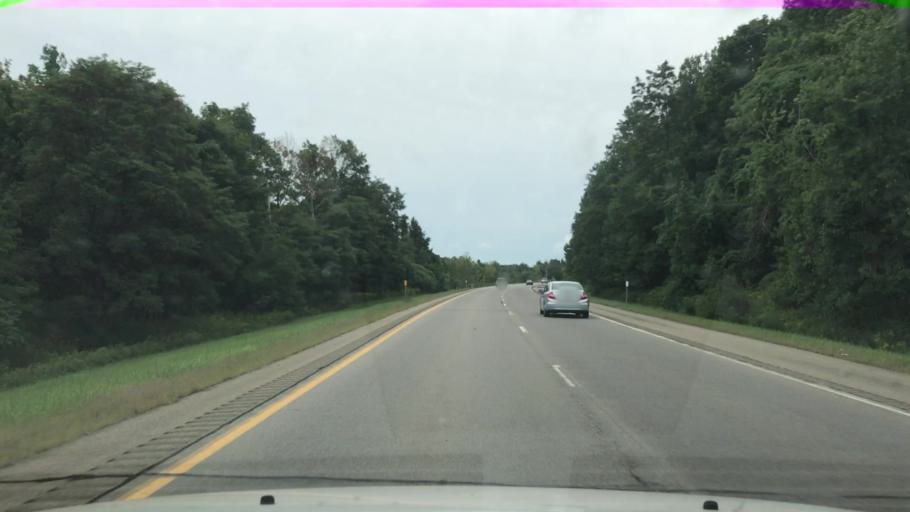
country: US
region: New York
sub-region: Erie County
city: Springville
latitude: 42.5715
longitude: -78.7159
